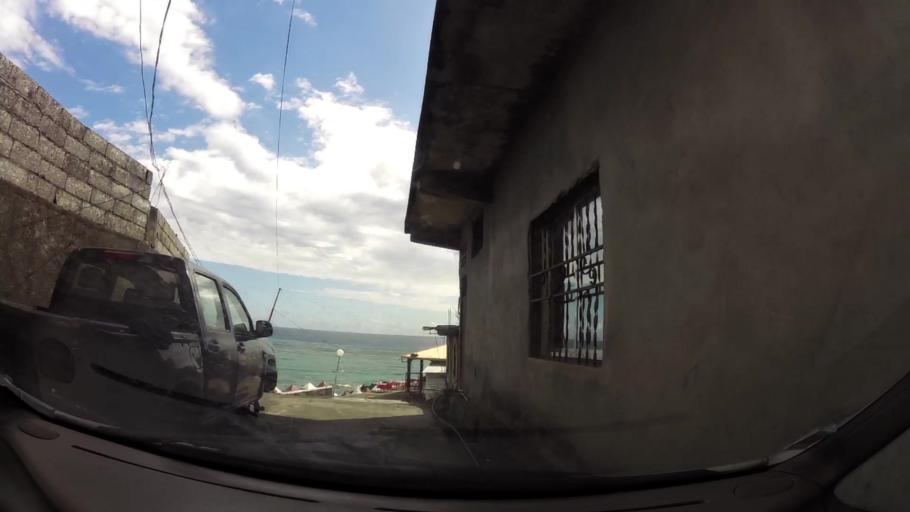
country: KM
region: Grande Comore
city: Itsandra
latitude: -11.6716
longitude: 43.2664
